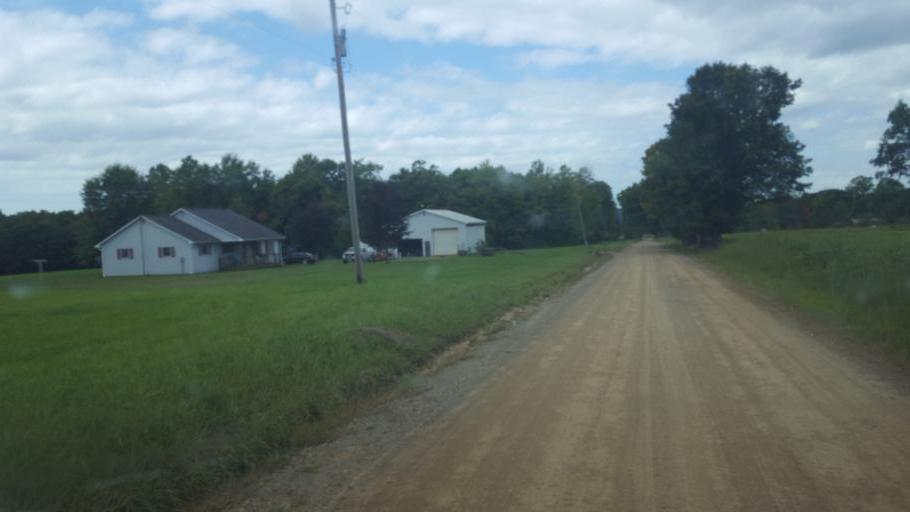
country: US
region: Pennsylvania
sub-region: Mercer County
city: Greenville
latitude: 41.4842
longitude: -80.3240
